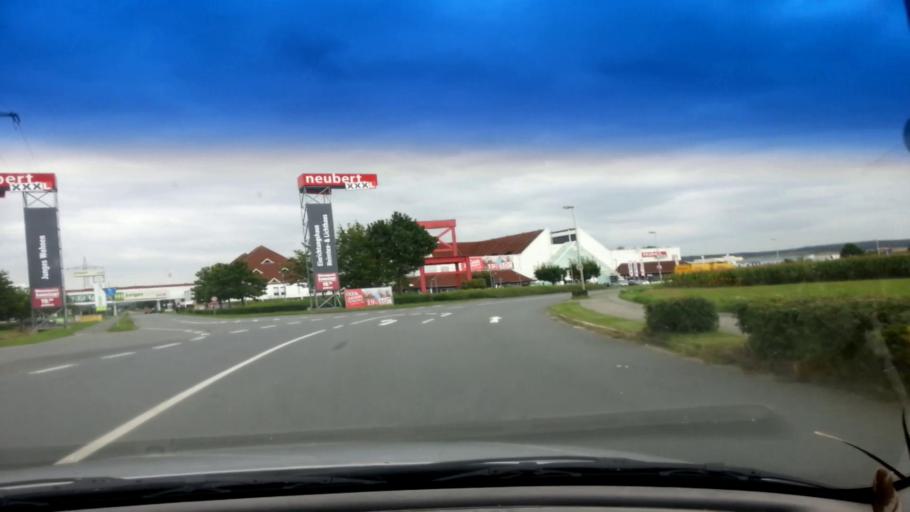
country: DE
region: Bavaria
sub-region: Upper Franconia
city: Hirschaid
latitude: 49.8180
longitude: 11.0015
